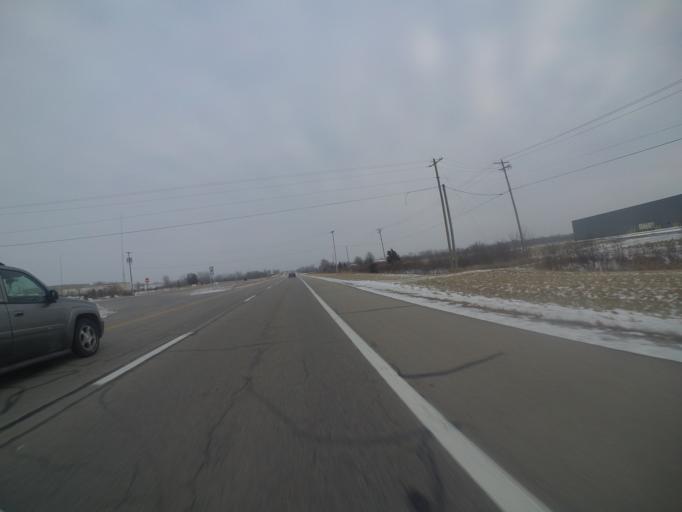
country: US
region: Ohio
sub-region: Wood County
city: Walbridge
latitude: 41.5637
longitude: -83.5249
